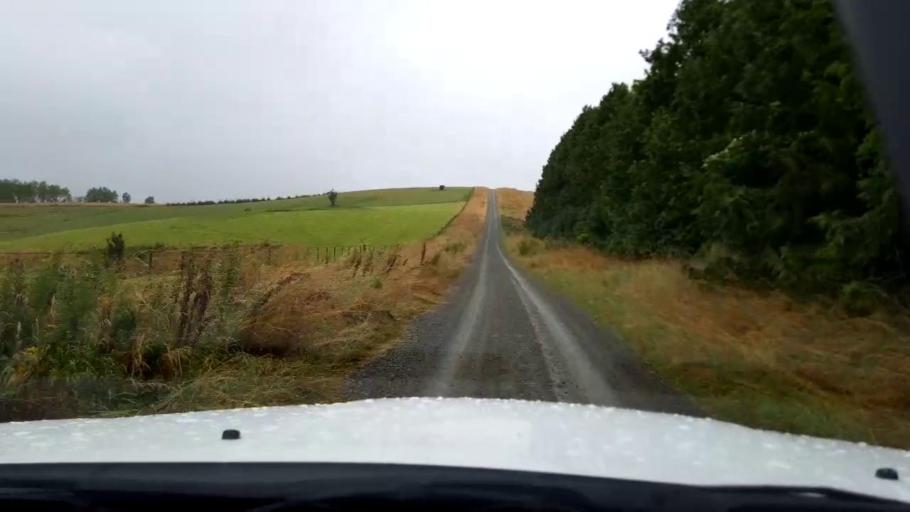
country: NZ
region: Canterbury
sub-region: Timaru District
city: Pleasant Point
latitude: -44.1734
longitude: 171.0942
